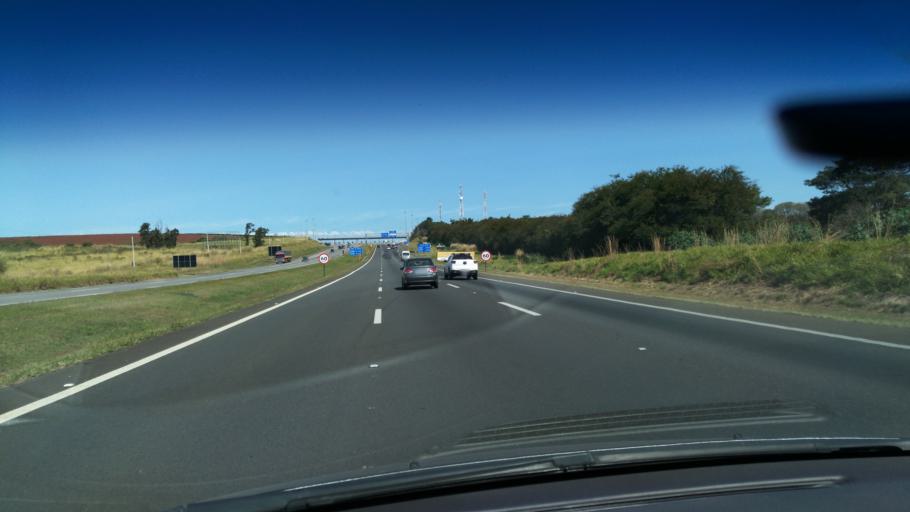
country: BR
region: Sao Paulo
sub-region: Jaguariuna
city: Jaguariuna
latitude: -22.7634
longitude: -47.0216
